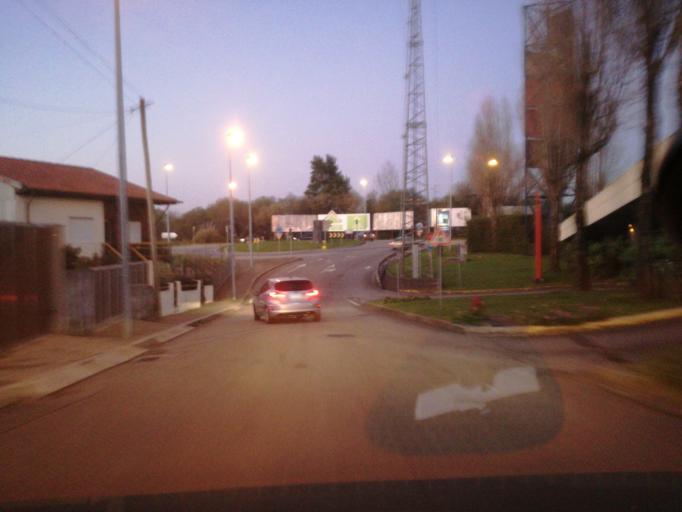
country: PT
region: Porto
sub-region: Valongo
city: Ermesinde
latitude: 41.2206
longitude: -8.5634
